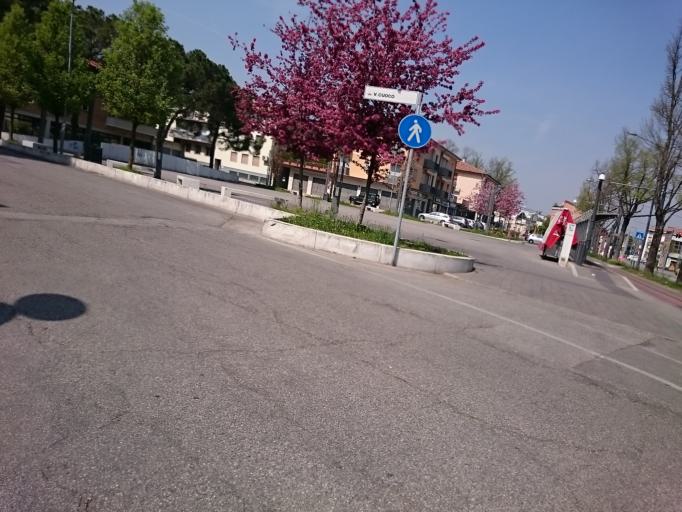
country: IT
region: Veneto
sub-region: Provincia di Padova
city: Mandriola-Sant'Agostino
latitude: 45.3797
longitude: 11.8698
